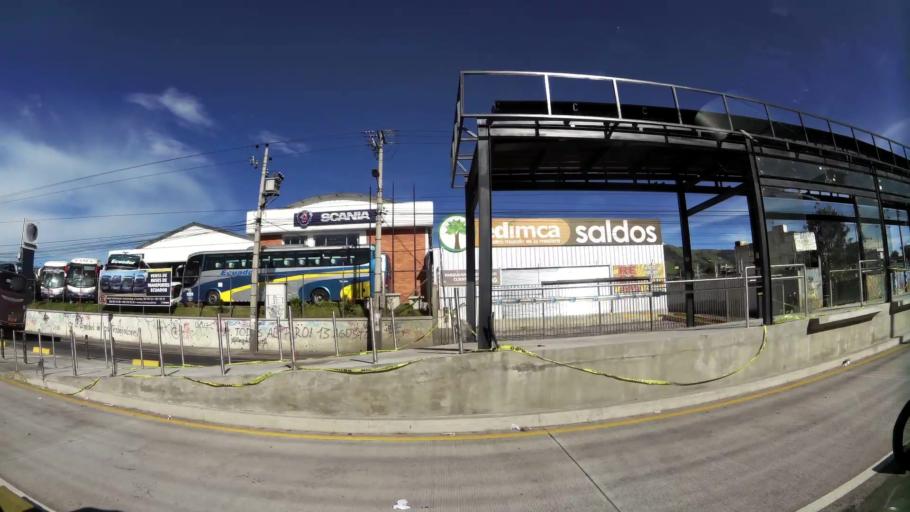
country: EC
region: Pichincha
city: Sangolqui
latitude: -0.3325
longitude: -78.5504
